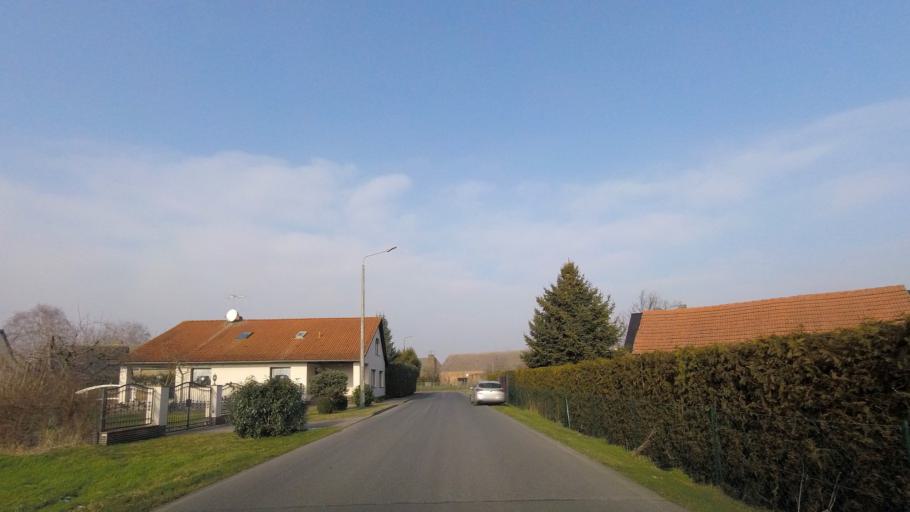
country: DE
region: Brandenburg
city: Niedergorsdorf
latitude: 51.9281
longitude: 13.0347
